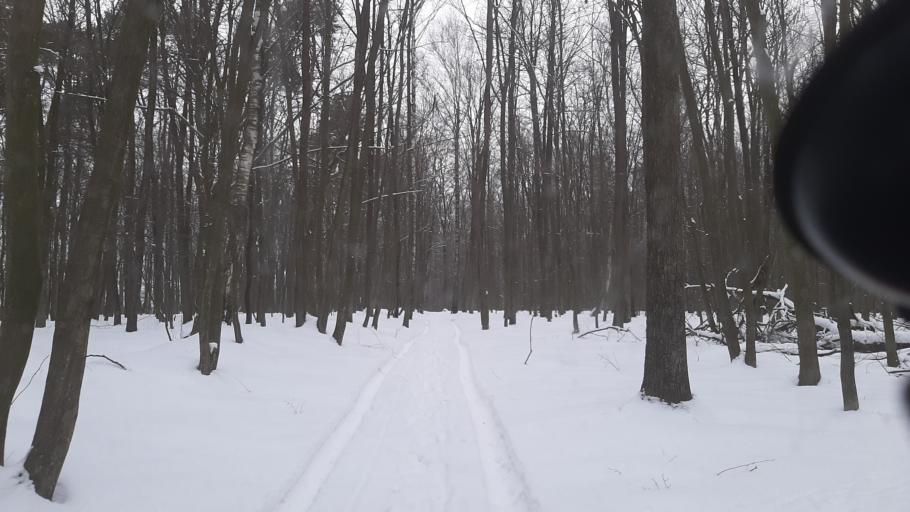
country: PL
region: Lublin Voivodeship
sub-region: Powiat lubelski
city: Garbow
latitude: 51.3719
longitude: 22.3897
